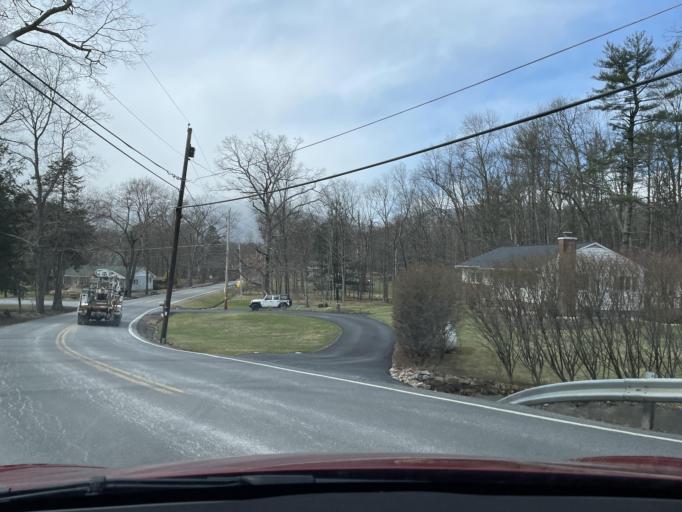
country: US
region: New York
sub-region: Ulster County
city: Manorville
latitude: 42.1102
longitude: -74.0034
